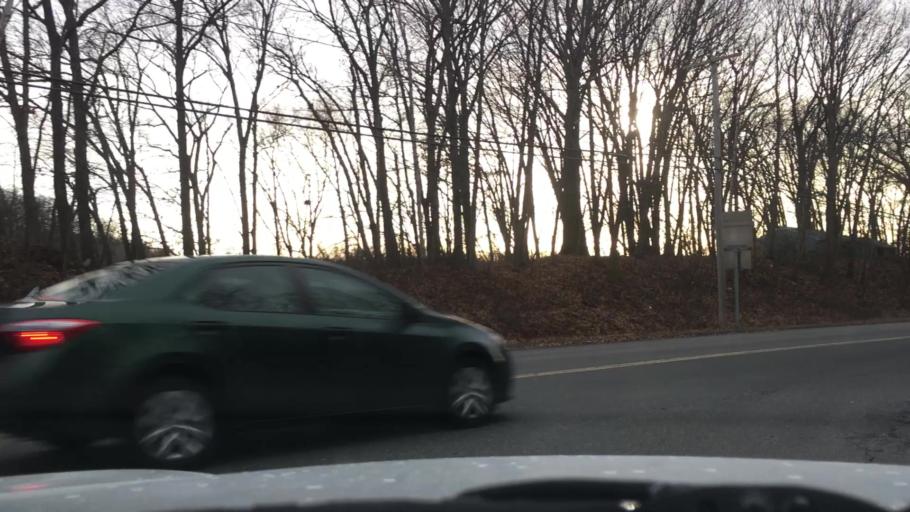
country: US
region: Massachusetts
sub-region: Hampden County
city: North Chicopee
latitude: 42.1599
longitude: -72.5451
